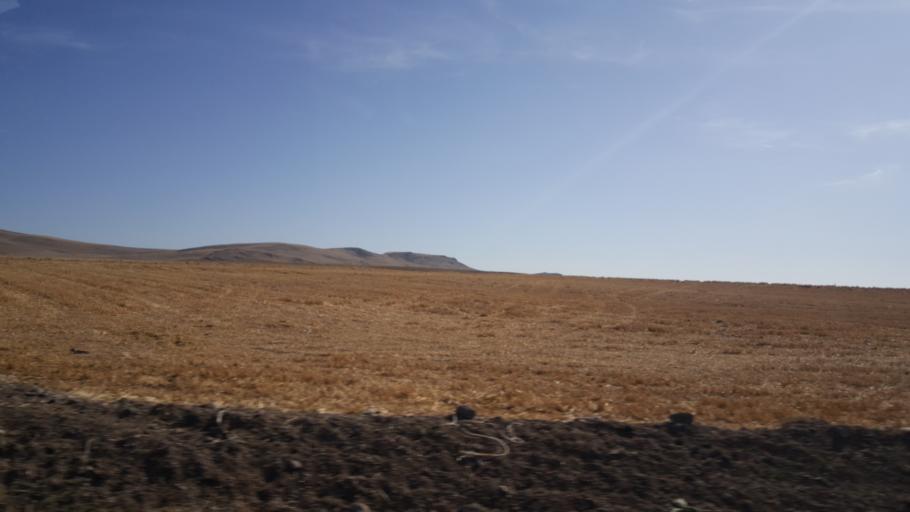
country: TR
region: Ankara
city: Yenice
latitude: 39.3535
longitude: 32.7850
